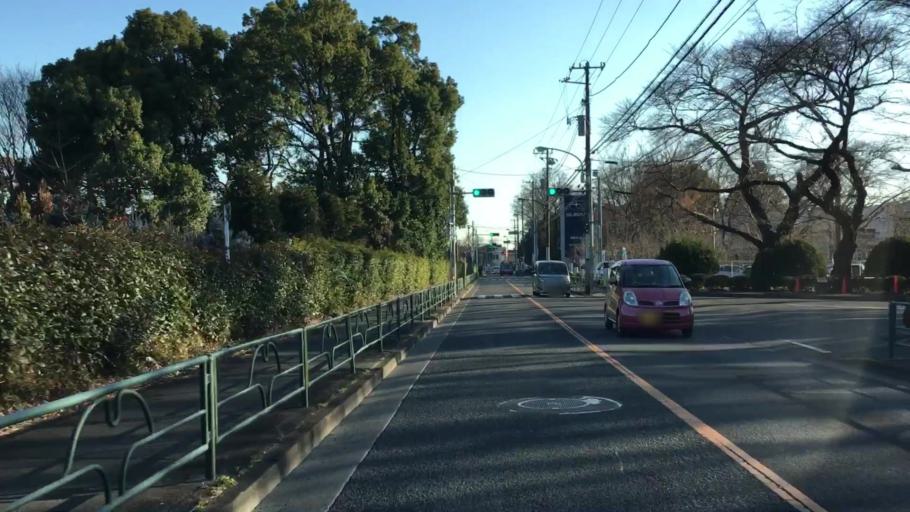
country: JP
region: Tokyo
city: Mitaka-shi
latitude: 35.6865
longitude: 139.5385
